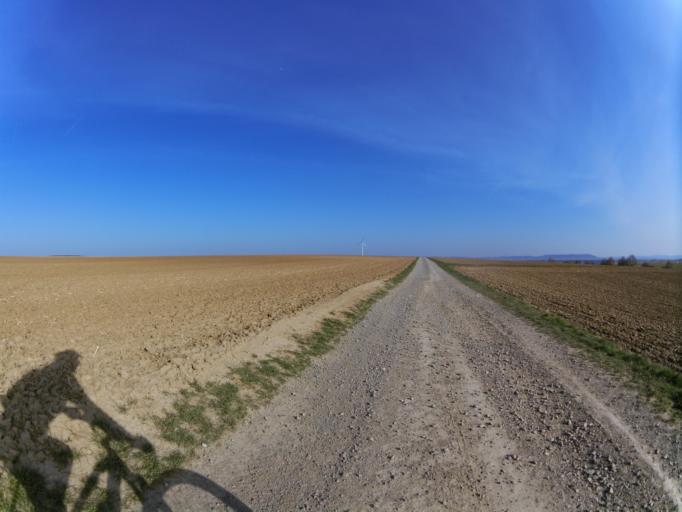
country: DE
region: Bavaria
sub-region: Regierungsbezirk Unterfranken
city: Prosselsheim
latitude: 49.8361
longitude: 10.1249
